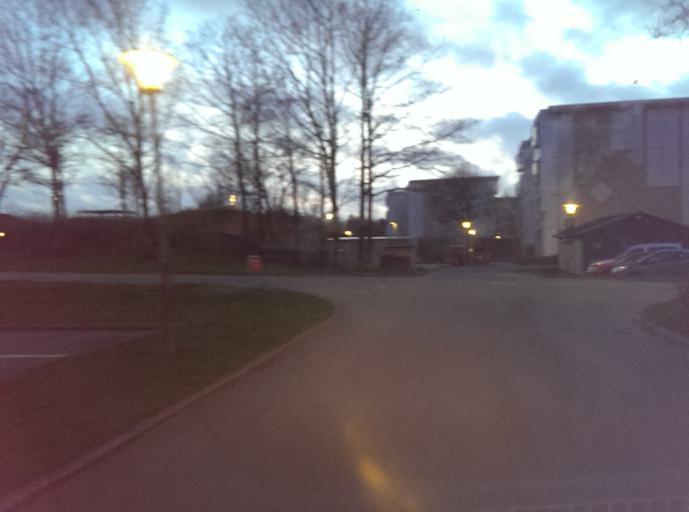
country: DK
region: South Denmark
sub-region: Esbjerg Kommune
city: Esbjerg
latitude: 55.4928
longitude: 8.4905
